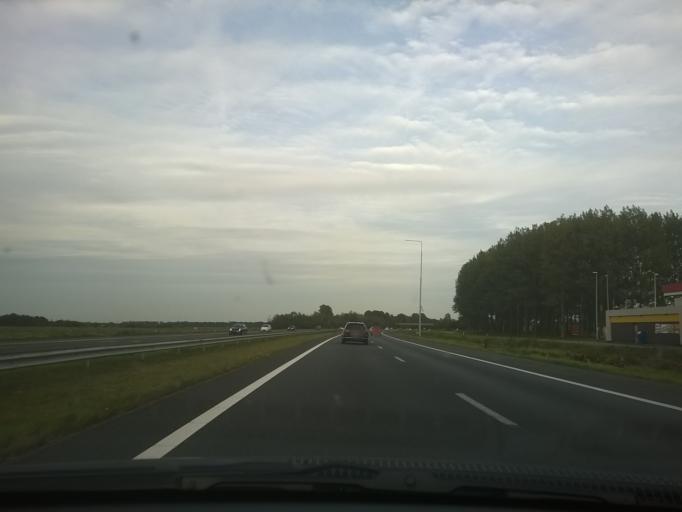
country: NL
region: Groningen
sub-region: Gemeente Grootegast
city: Grootegast
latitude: 53.1620
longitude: 6.2924
